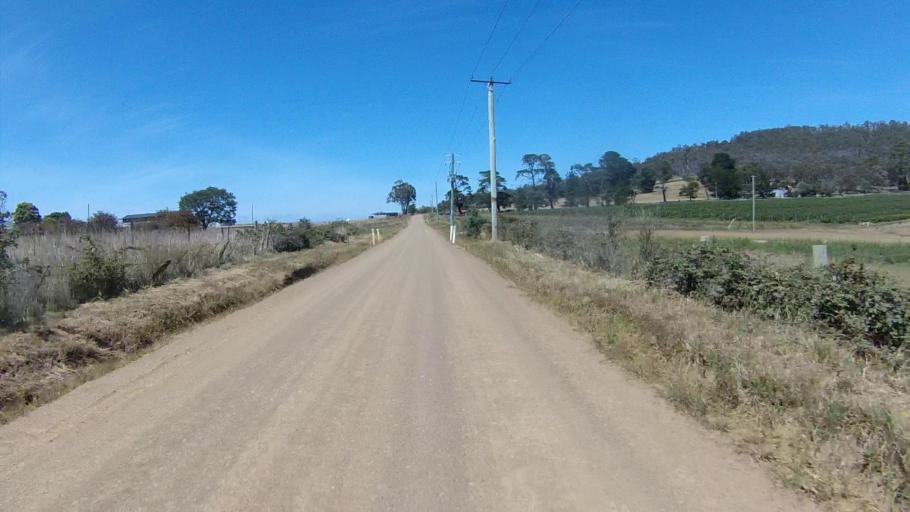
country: AU
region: Tasmania
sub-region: Sorell
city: Sorell
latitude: -42.7854
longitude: 147.6387
